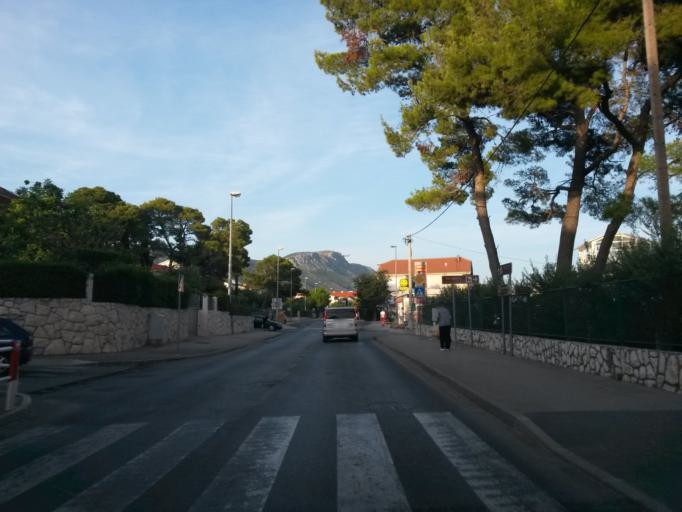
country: HR
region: Splitsko-Dalmatinska
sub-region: Grad Trogir
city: Trogir
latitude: 43.5510
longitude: 16.3347
